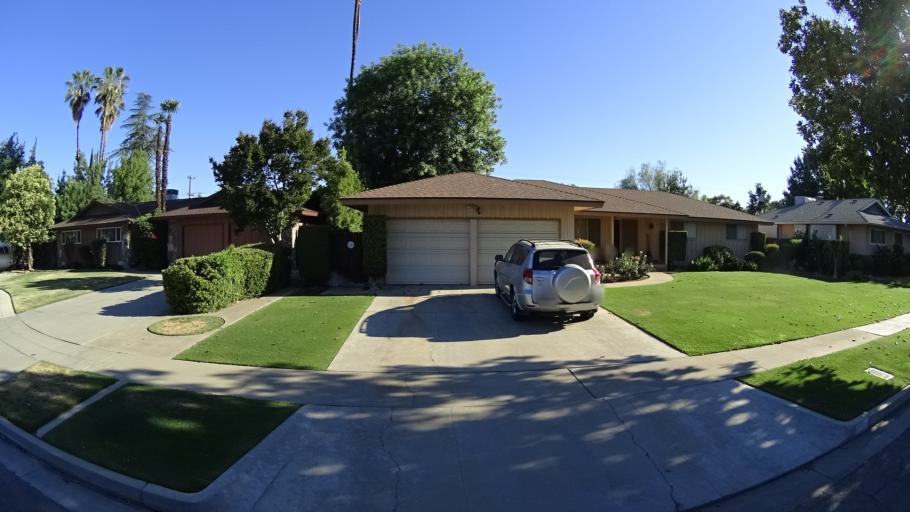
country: US
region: California
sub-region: Fresno County
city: Fresno
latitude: 36.8020
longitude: -119.8206
